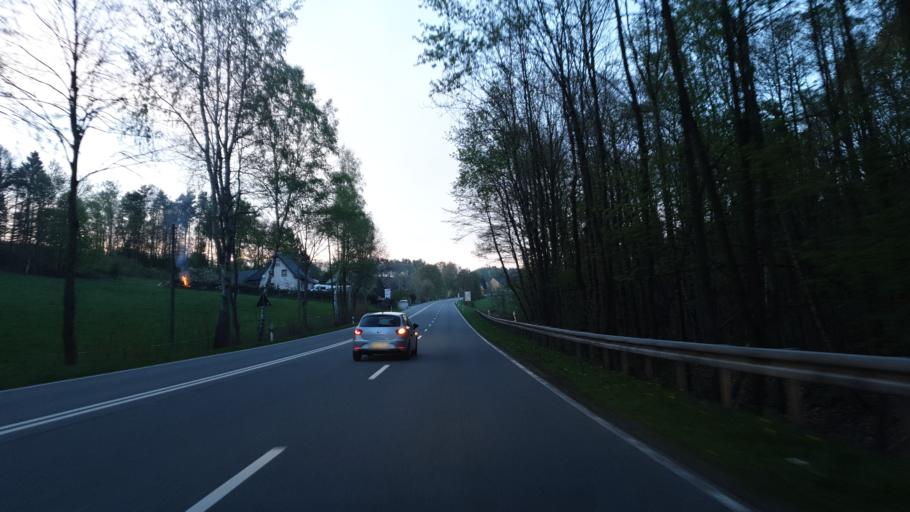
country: DE
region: Saxony
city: Lossnitz
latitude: 50.6360
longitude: 12.7334
